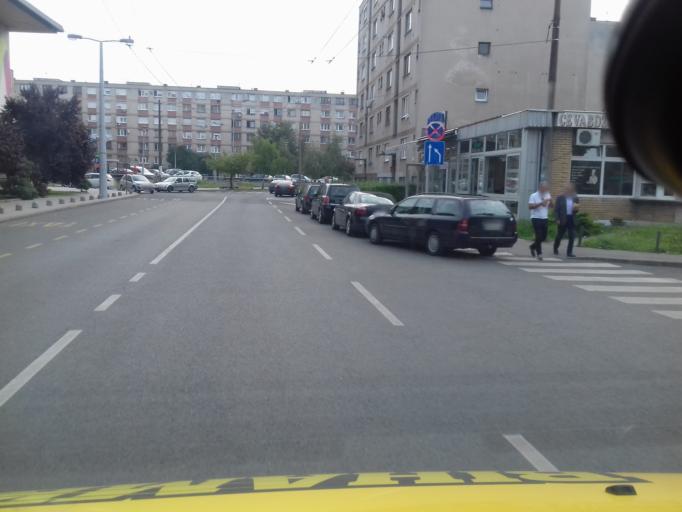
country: BA
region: Federation of Bosnia and Herzegovina
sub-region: Kanton Sarajevo
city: Sarajevo
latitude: 43.8480
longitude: 18.3678
